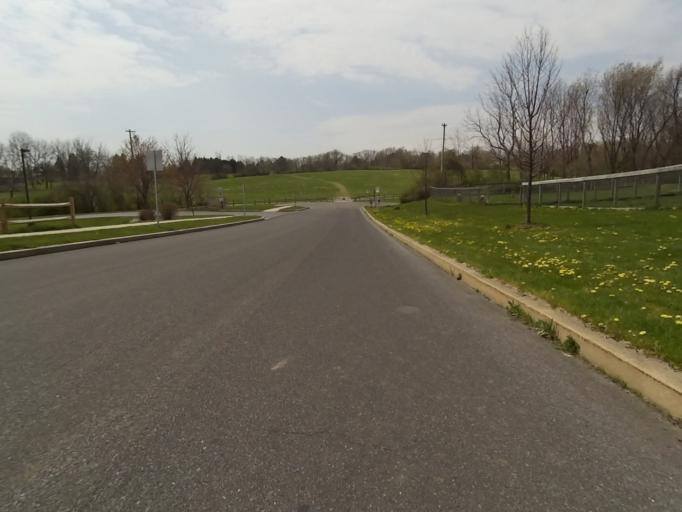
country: US
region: Pennsylvania
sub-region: Centre County
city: Park Forest Village
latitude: 40.8001
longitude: -77.8903
